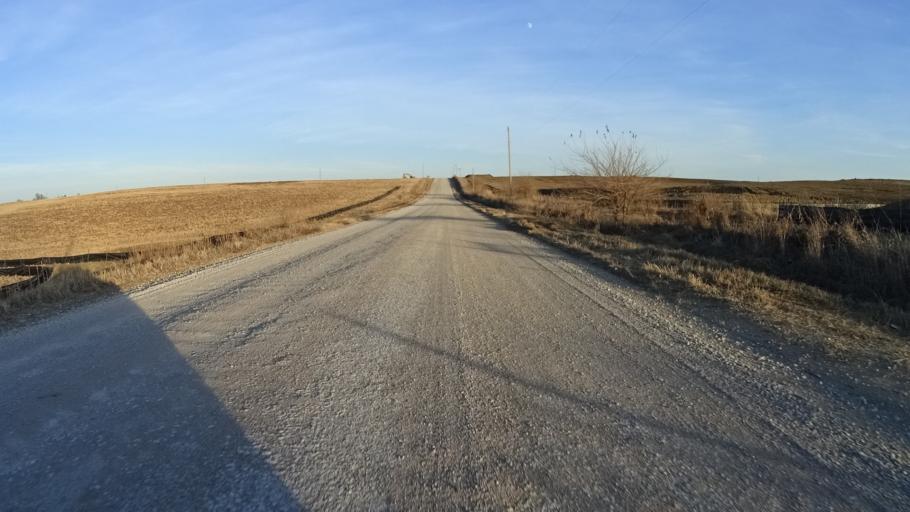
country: US
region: Nebraska
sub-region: Sarpy County
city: Papillion
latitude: 41.1326
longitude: -96.0993
